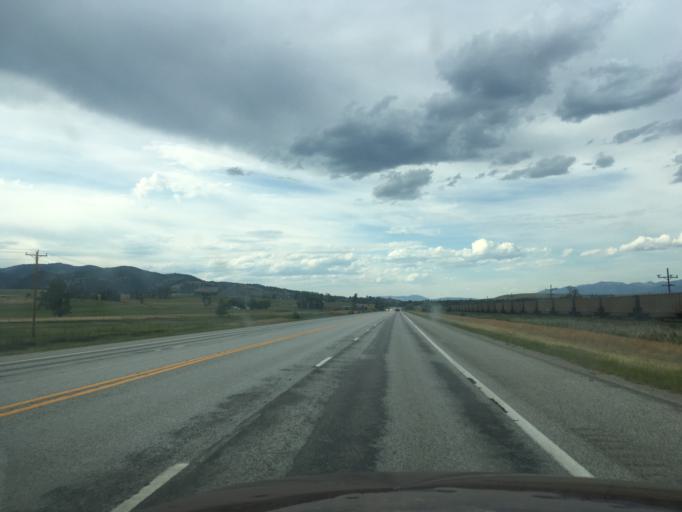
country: US
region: Montana
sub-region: Missoula County
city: Lolo
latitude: 46.7286
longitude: -114.0791
